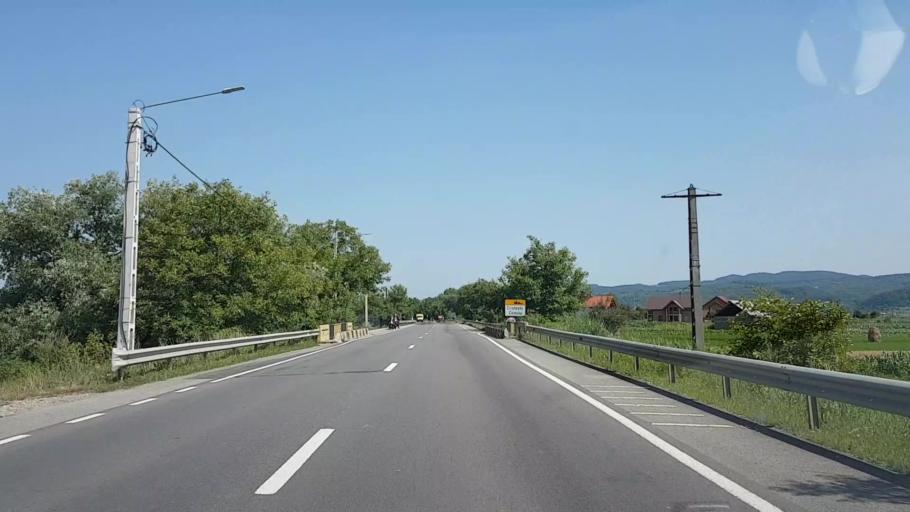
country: RO
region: Bistrita-Nasaud
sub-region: Comuna Uriu
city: Cristestii Ciceului
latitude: 47.1971
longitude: 24.0788
